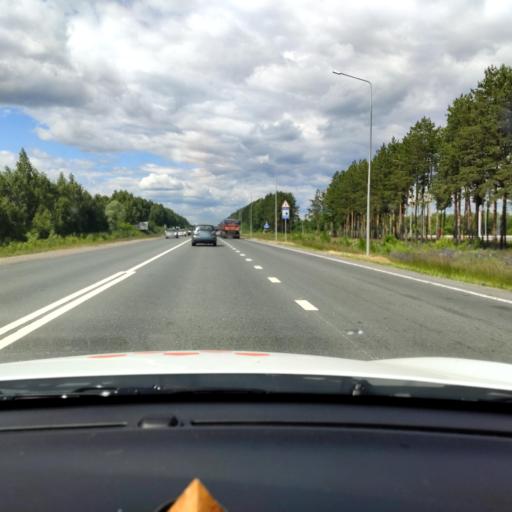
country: RU
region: Mariy-El
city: Pomary
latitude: 55.9427
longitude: 48.3702
